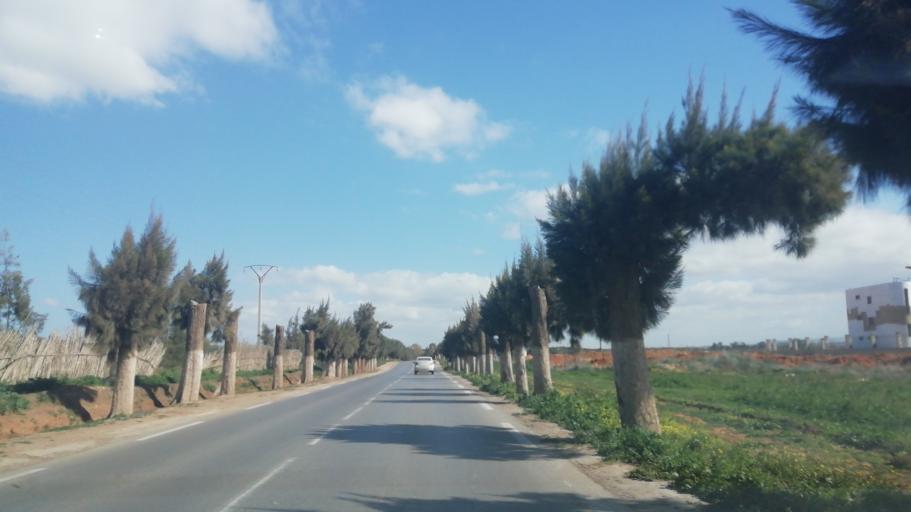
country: DZ
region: Mostaganem
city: Mostaganem
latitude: 35.9993
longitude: 0.3110
